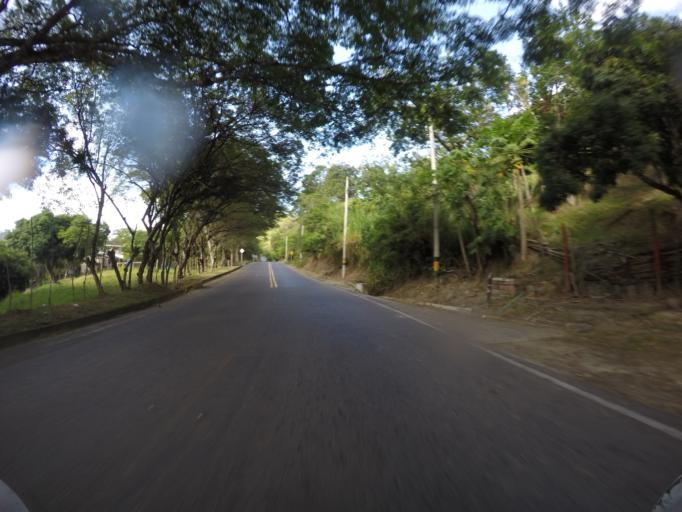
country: CO
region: Valle del Cauca
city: Cartago
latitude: 4.7259
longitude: -75.8731
